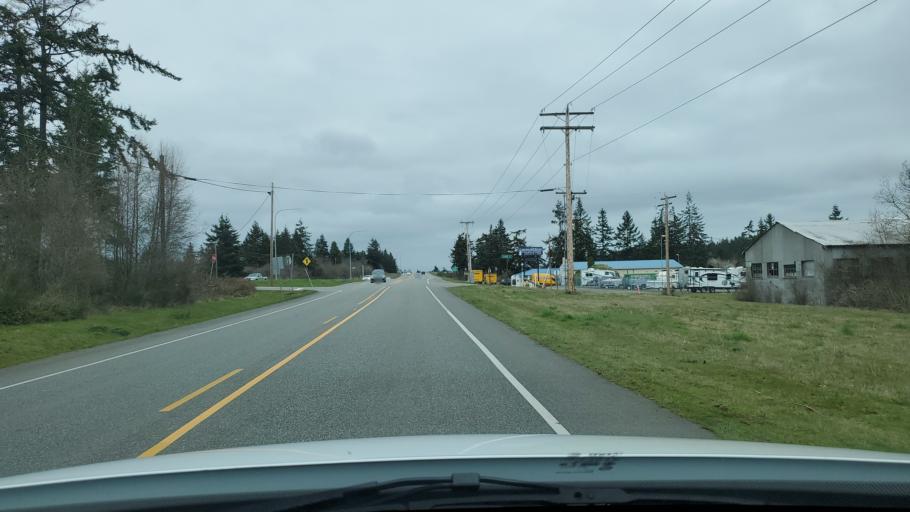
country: US
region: Washington
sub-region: Island County
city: Oak Harbor
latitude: 48.3178
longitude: -122.6299
